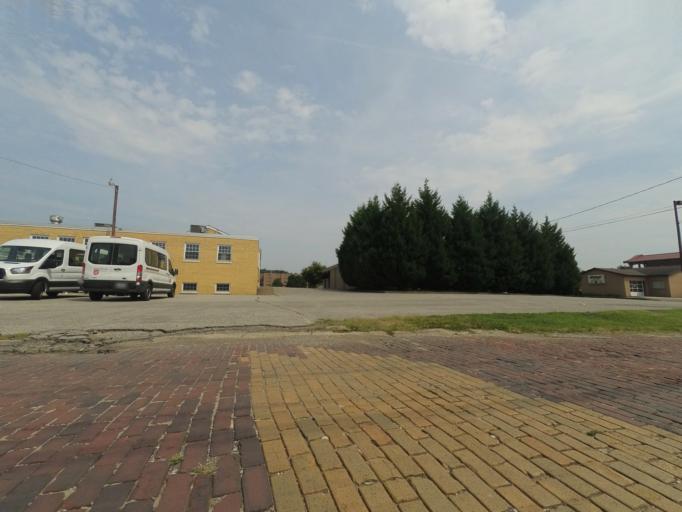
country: US
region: West Virginia
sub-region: Cabell County
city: Huntington
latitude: 38.4225
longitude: -82.4376
